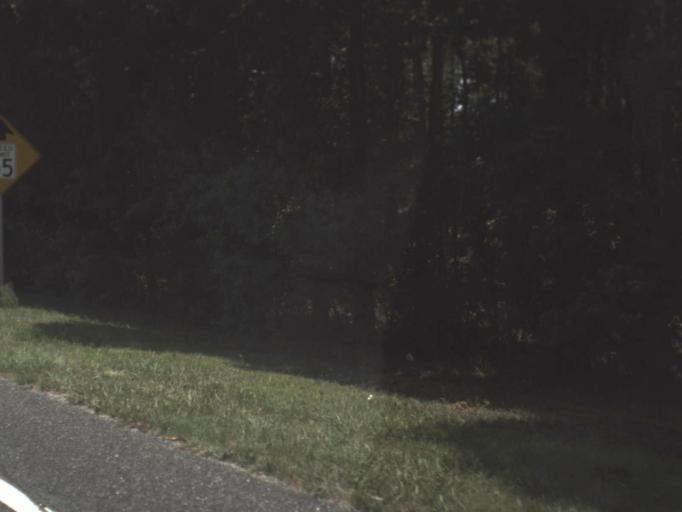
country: US
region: Florida
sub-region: Dixie County
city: Cross City
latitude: 29.6456
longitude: -83.1533
